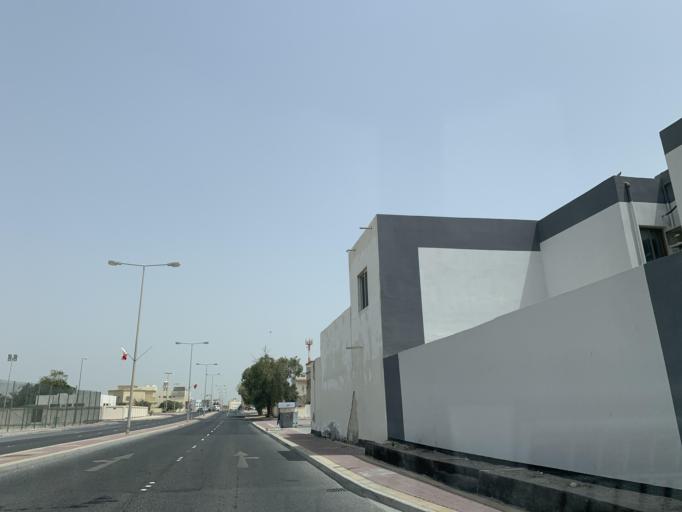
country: BH
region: Northern
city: Madinat `Isa
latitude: 26.1663
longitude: 50.5559
